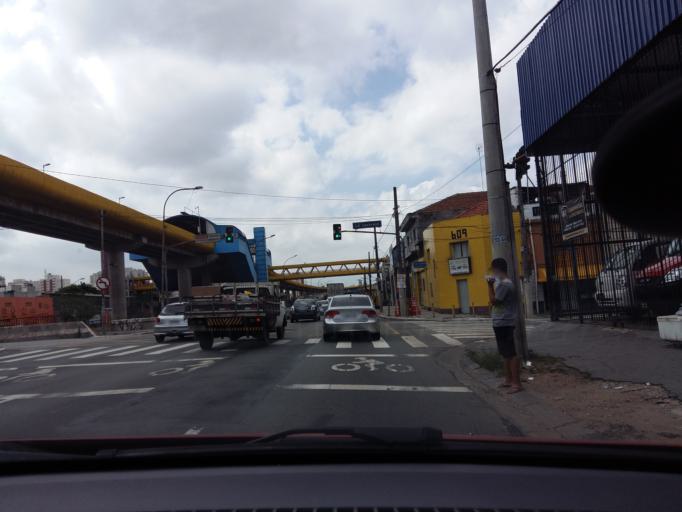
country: BR
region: Sao Paulo
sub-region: Sao Caetano Do Sul
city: Sao Caetano do Sul
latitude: -23.5926
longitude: -46.5975
